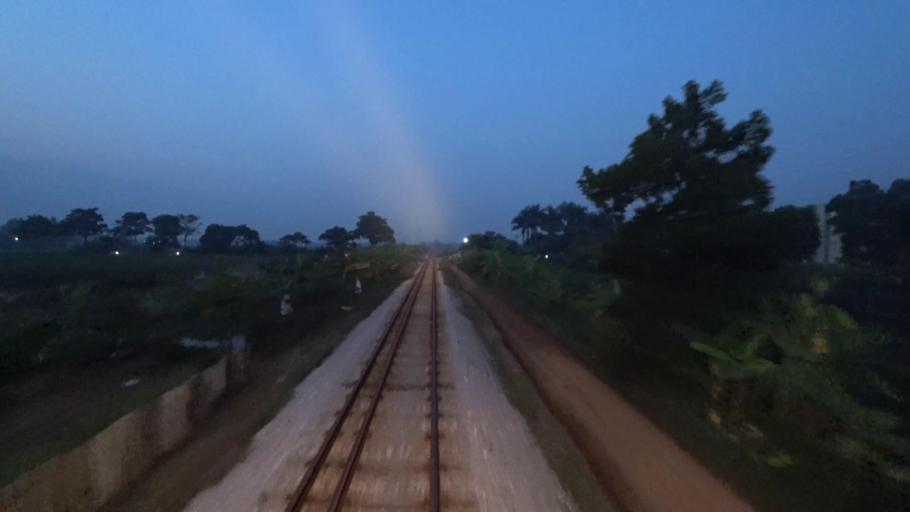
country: VN
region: Ha Noi
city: Soc Son
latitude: 21.2629
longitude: 105.8621
